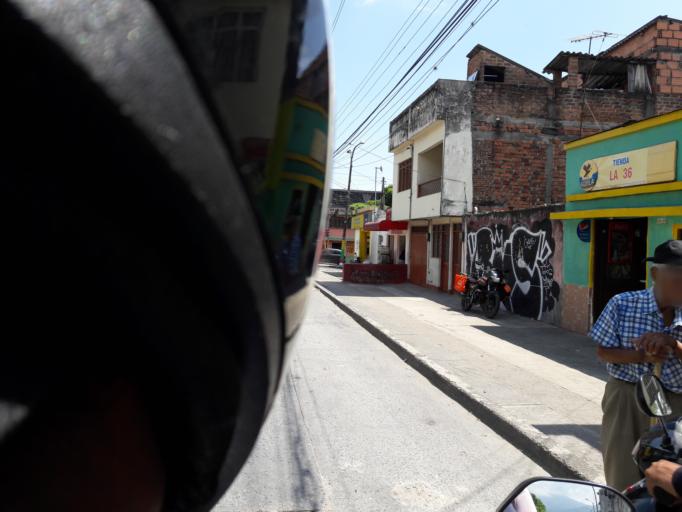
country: CO
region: Tolima
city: Ibague
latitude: 4.4348
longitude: -75.2180
